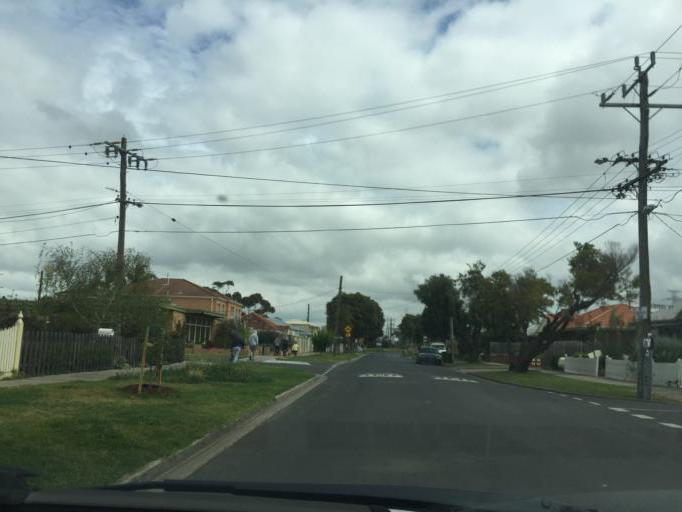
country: AU
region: Victoria
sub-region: Hobsons Bay
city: South Kingsville
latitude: -37.8262
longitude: 144.8718
